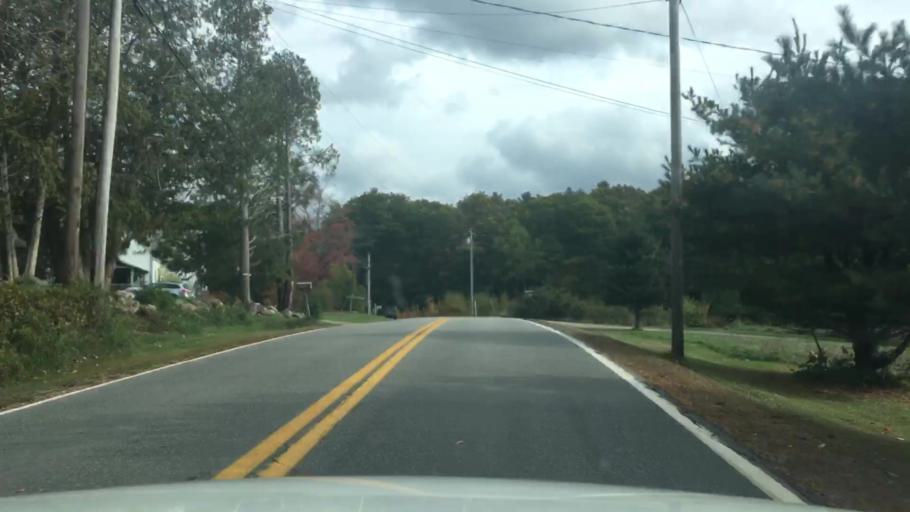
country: US
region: Maine
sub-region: Knox County
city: Hope
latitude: 44.2890
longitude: -69.1189
